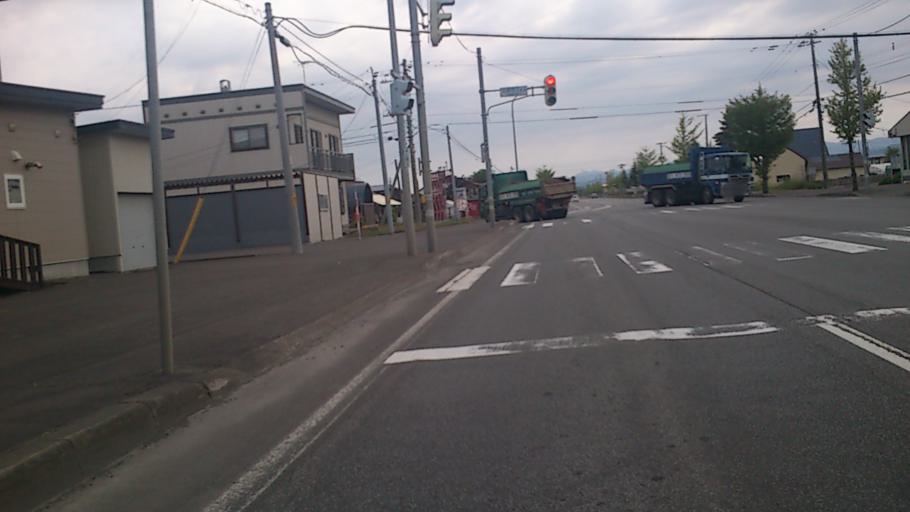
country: JP
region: Hokkaido
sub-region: Asahikawa-shi
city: Asahikawa
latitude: 43.8351
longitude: 142.4733
